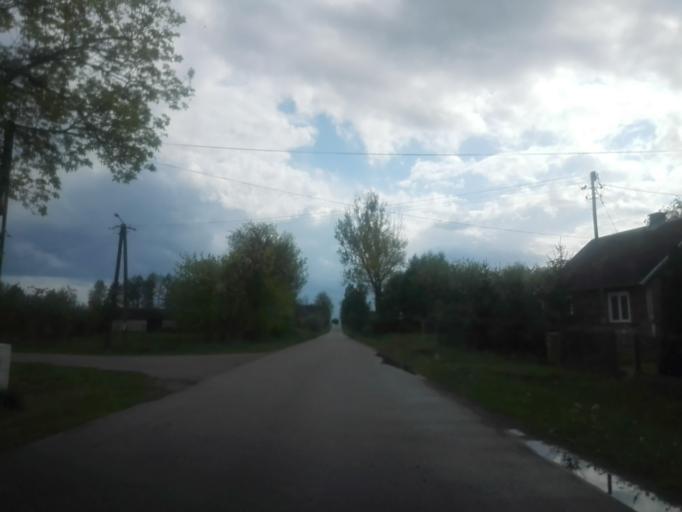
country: PL
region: Podlasie
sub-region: Powiat lomzynski
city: Wizna
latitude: 53.2639
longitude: 22.4491
